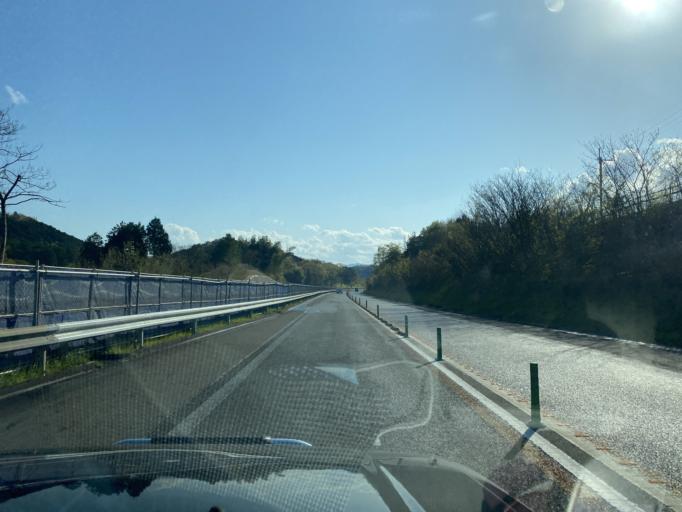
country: JP
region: Kyoto
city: Ayabe
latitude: 35.3262
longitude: 135.2221
